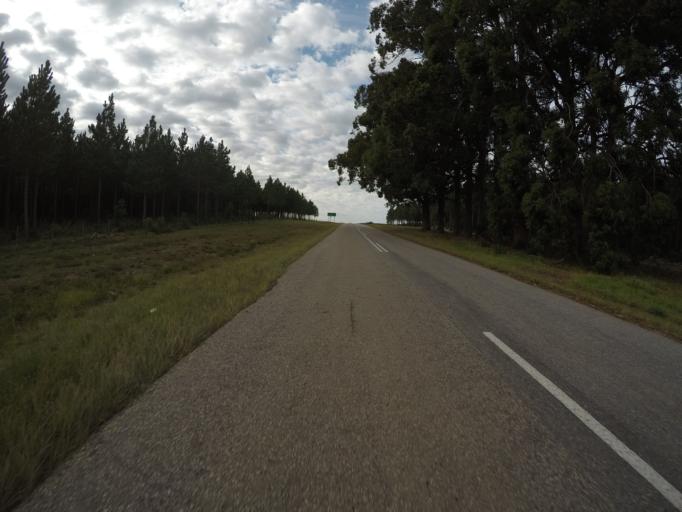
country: ZA
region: Eastern Cape
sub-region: Cacadu District Municipality
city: Kareedouw
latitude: -34.0289
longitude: 24.3766
